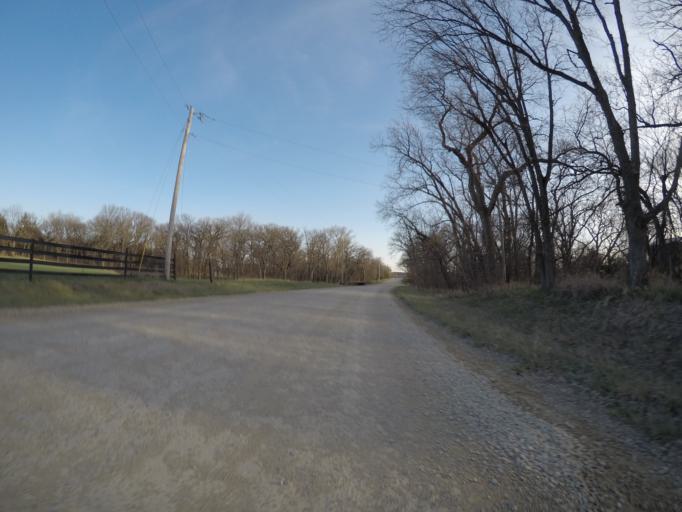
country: US
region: Kansas
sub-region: Riley County
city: Ogden
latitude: 39.2254
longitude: -96.7007
